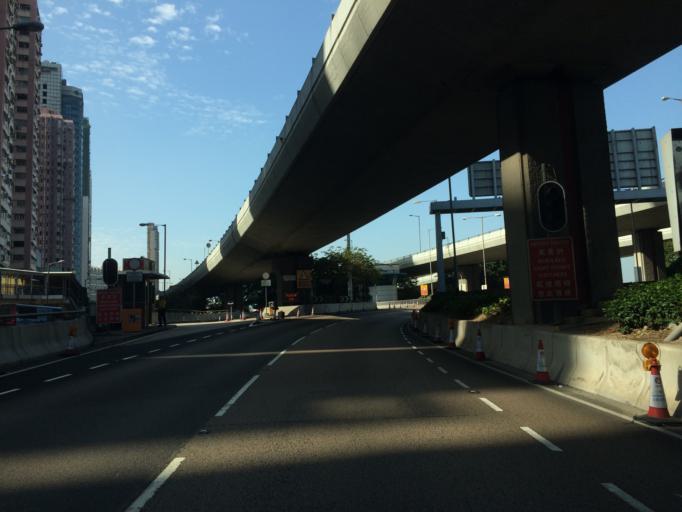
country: HK
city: Hong Kong
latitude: 22.2888
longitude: 114.1415
